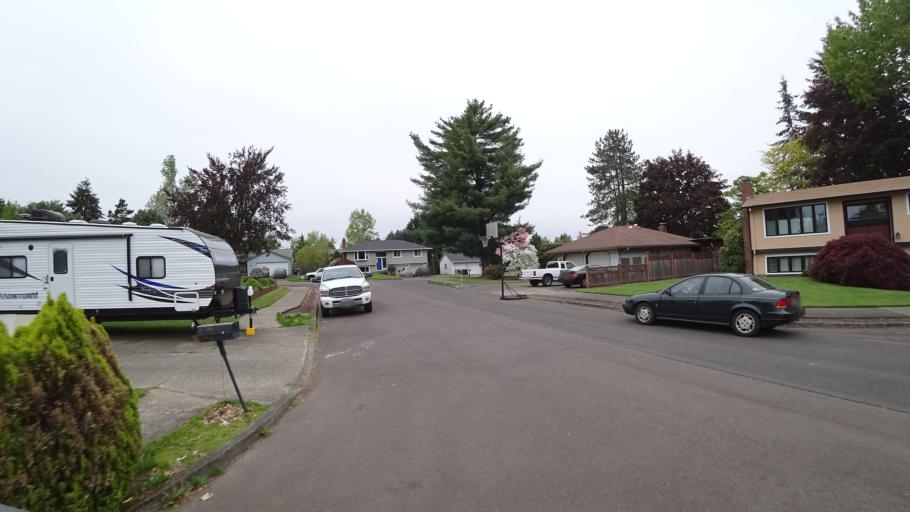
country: US
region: Oregon
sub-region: Washington County
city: Aloha
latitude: 45.5024
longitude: -122.8767
